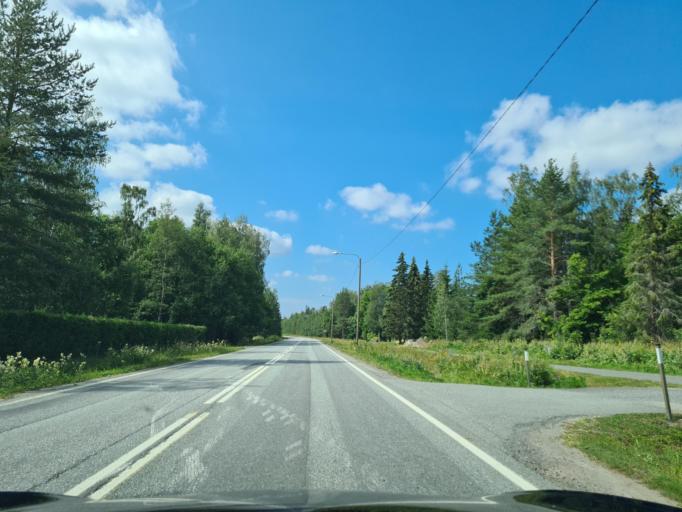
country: FI
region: Ostrobothnia
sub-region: Vaasa
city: Vaasa
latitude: 63.1937
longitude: 21.5564
